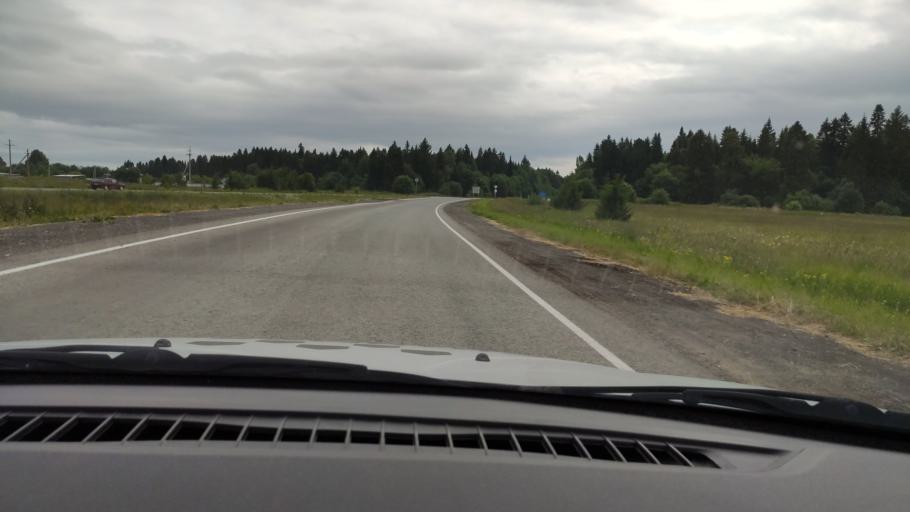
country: RU
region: Perm
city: Kungur
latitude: 57.4018
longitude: 56.8837
